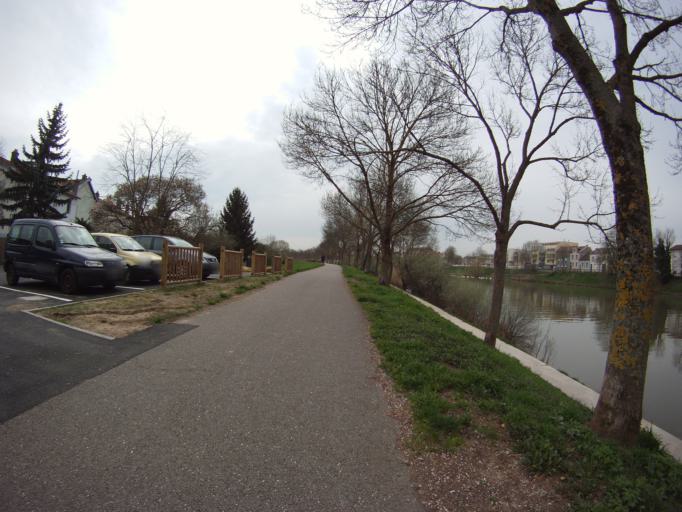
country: FR
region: Lorraine
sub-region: Departement de Meurthe-et-Moselle
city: Malzeville
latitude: 48.7080
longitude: 6.1813
